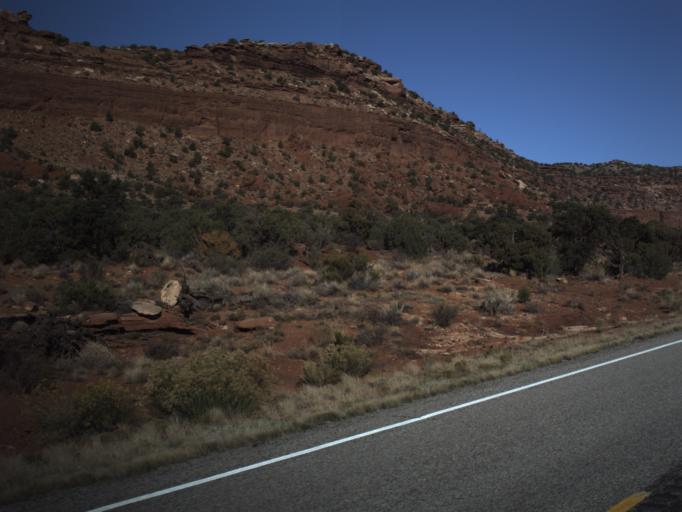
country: US
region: Utah
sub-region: San Juan County
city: Blanding
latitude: 37.6084
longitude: -110.0799
